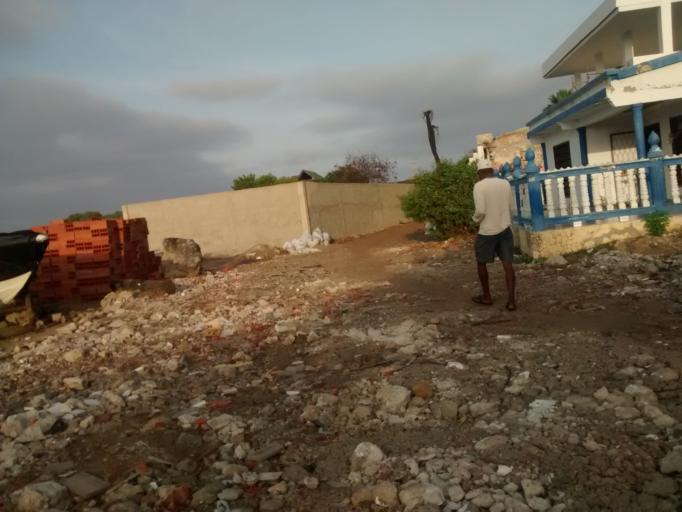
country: CO
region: Bolivar
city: Turbana
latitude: 10.1404
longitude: -75.6848
